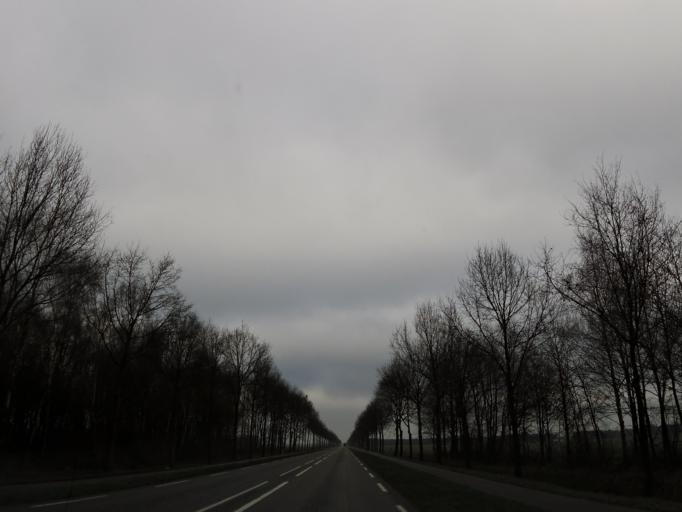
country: NL
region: Limburg
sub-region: Gemeente Peel en Maas
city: Maasbree
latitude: 51.3975
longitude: 5.9714
